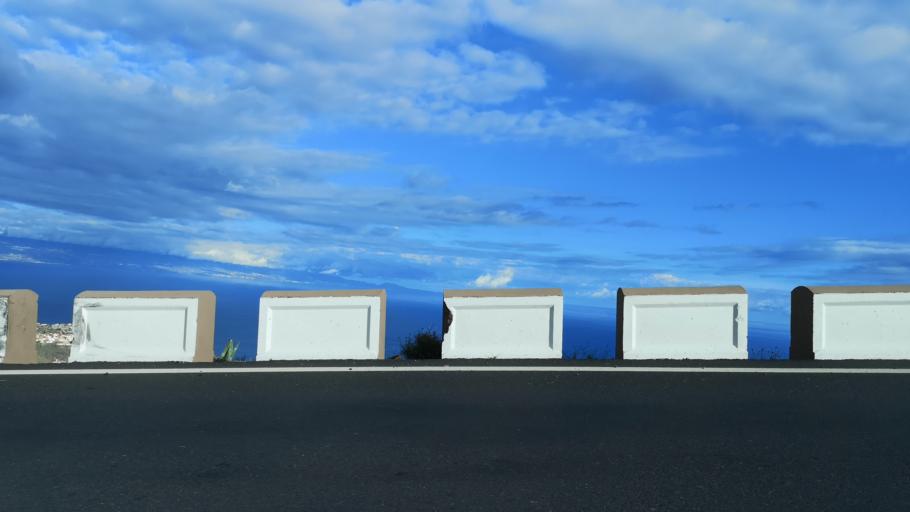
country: ES
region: Canary Islands
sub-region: Provincia de Santa Cruz de Tenerife
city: San Sebastian de la Gomera
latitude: 28.0856
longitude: -17.1429
